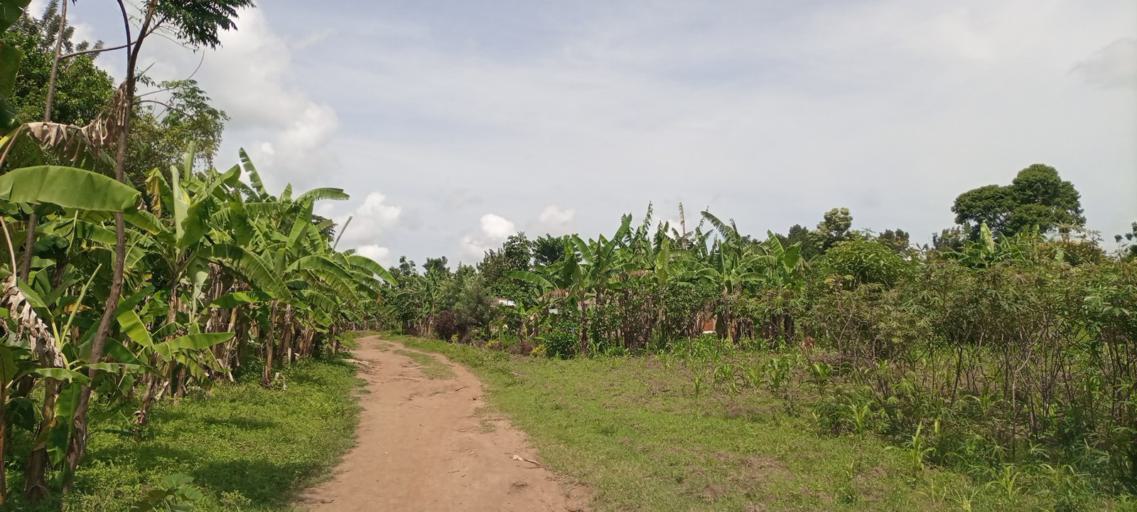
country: UG
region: Eastern Region
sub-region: Budaka District
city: Budaka
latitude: 1.1709
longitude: 33.9465
